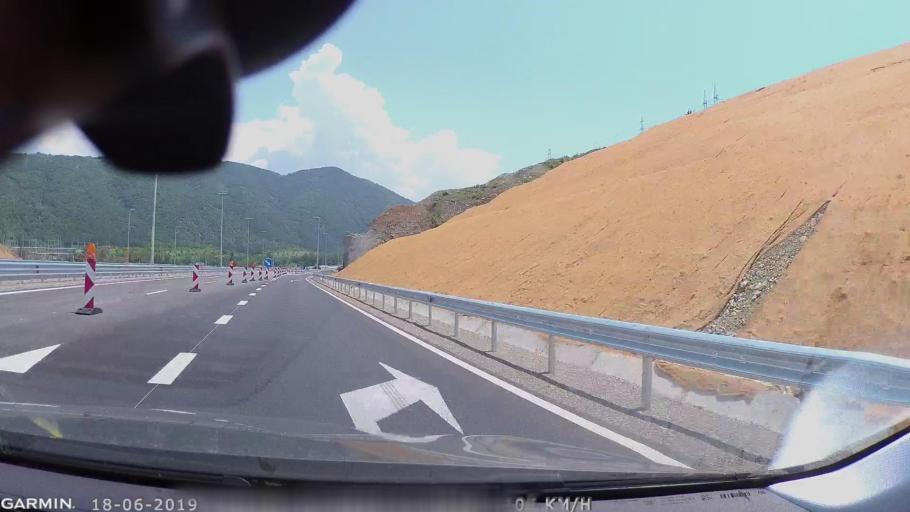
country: BG
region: Blagoevgrad
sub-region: Obshtina Blagoevgrad
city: Blagoevgrad
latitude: 41.9661
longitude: 23.0933
